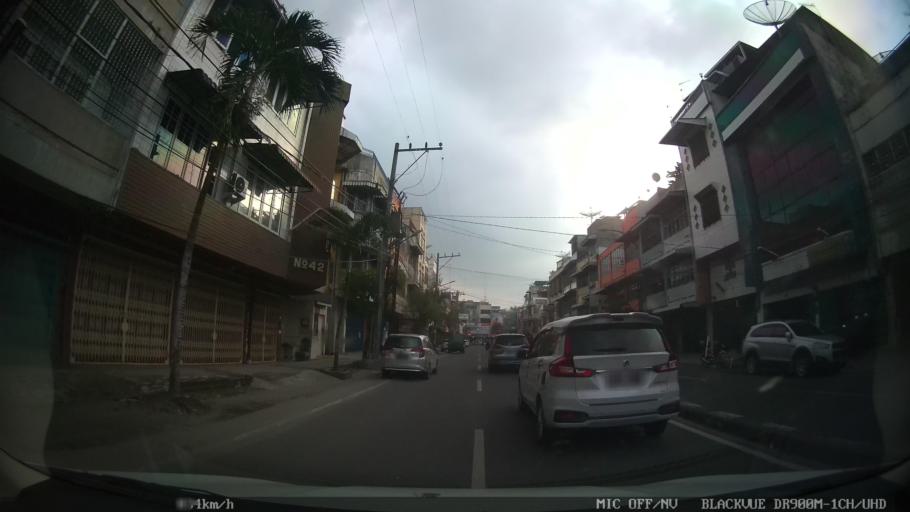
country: ID
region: North Sumatra
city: Medan
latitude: 3.5805
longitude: 98.6903
